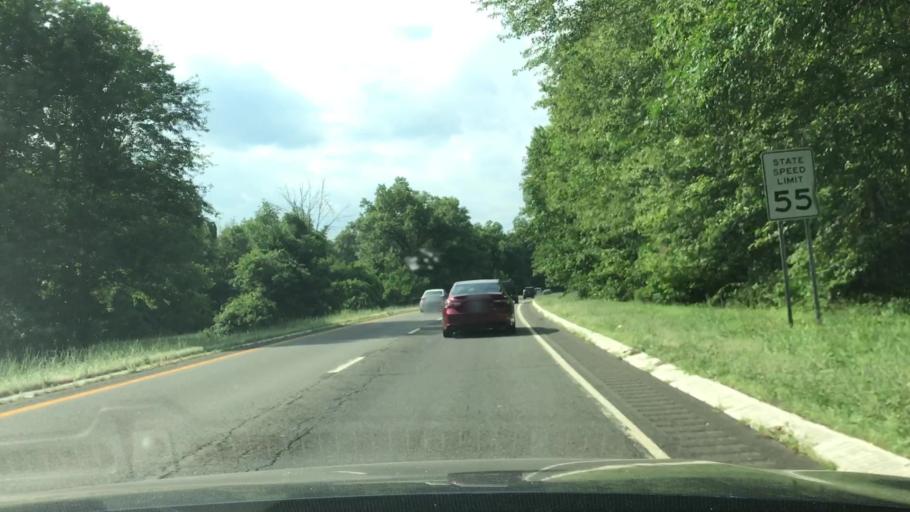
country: US
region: New York
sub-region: Rockland County
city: Bardonia
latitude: 41.1108
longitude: -74.0005
